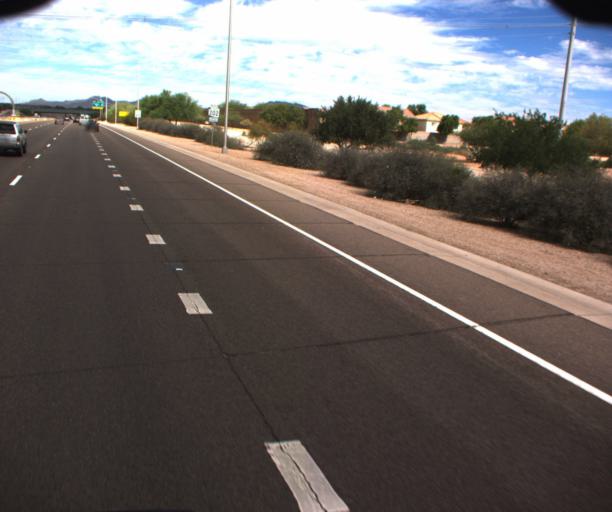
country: US
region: Arizona
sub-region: Maricopa County
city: Queen Creek
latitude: 33.3570
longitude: -111.6438
